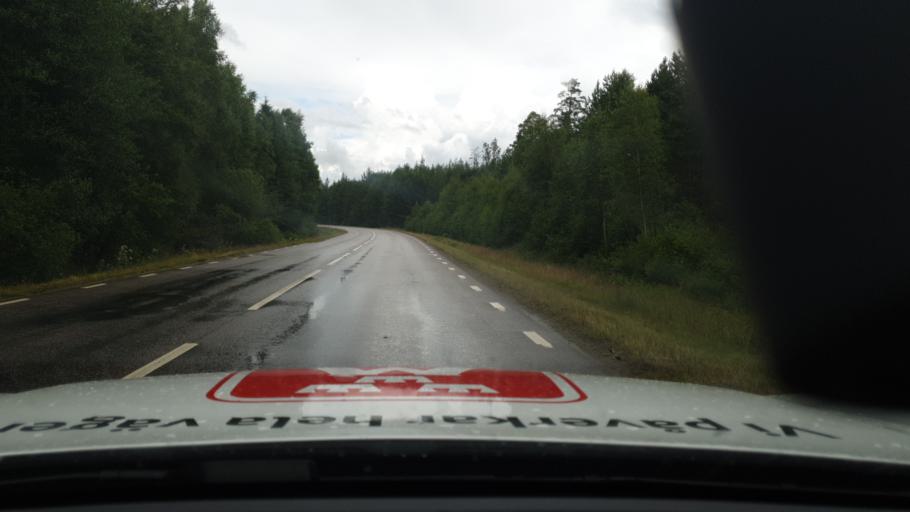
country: SE
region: Vaestra Goetaland
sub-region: Karlsborgs Kommun
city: Molltorp
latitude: 58.6138
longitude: 14.3897
